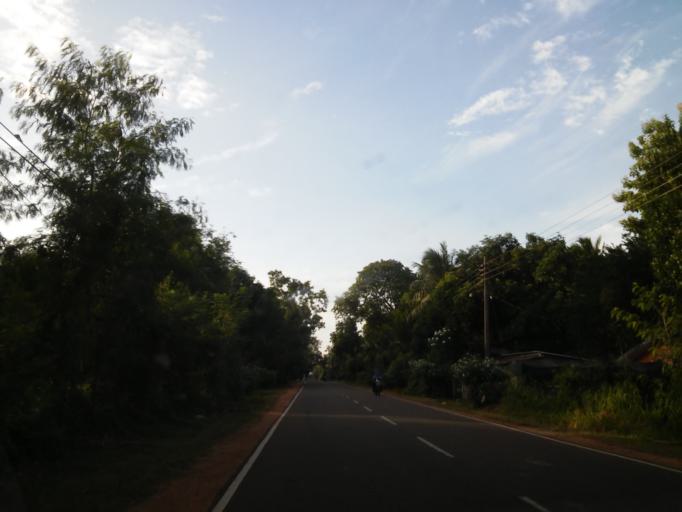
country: LK
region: North Central
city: Anuradhapura
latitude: 8.1239
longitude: 80.5679
